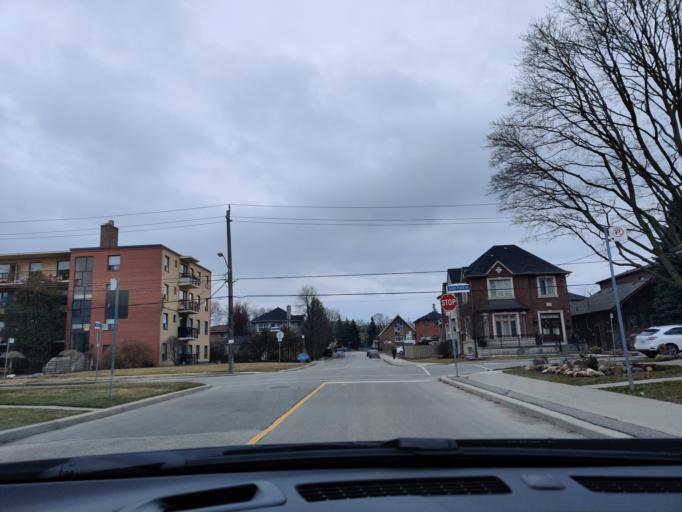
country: CA
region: Ontario
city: Toronto
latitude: 43.7079
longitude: -79.4561
